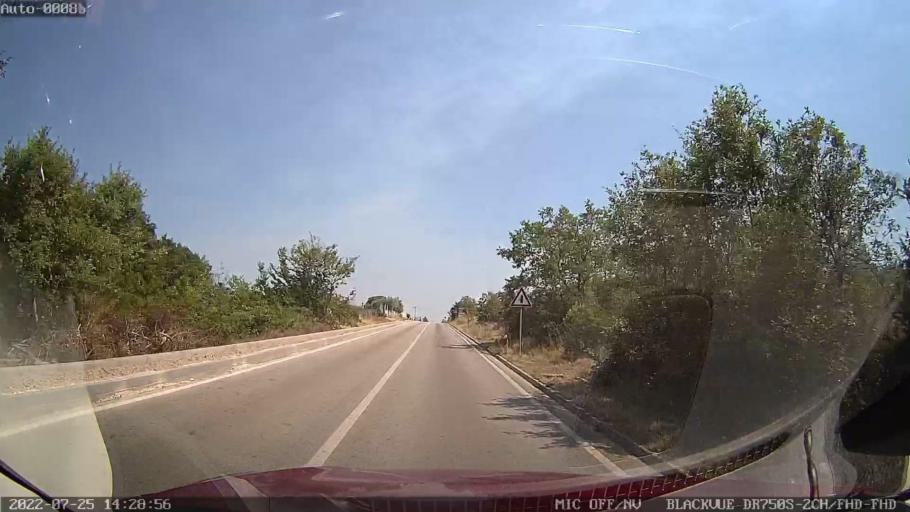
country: HR
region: Zadarska
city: Policnik
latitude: 44.1231
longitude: 15.3521
